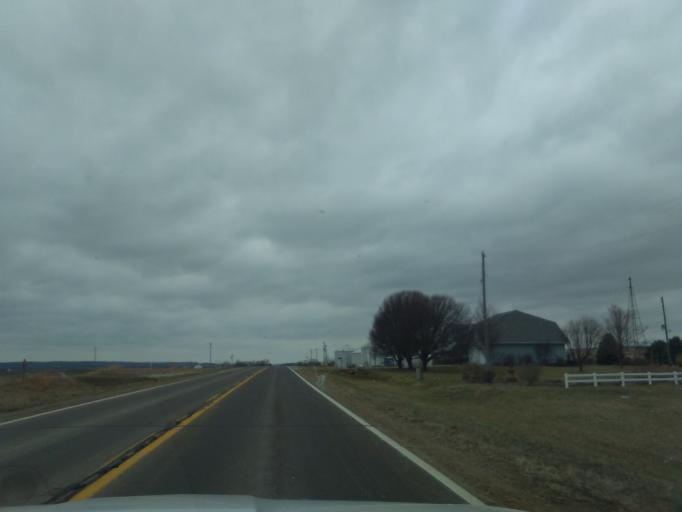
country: US
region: Nebraska
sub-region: Richardson County
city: Falls City
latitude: 40.0657
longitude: -95.6306
